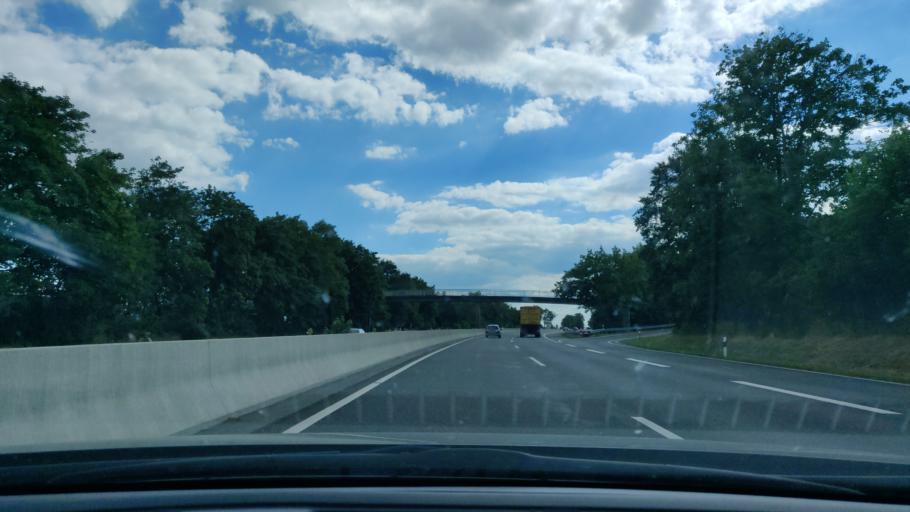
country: DE
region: Hesse
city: Gudensberg
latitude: 51.1926
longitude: 9.3963
